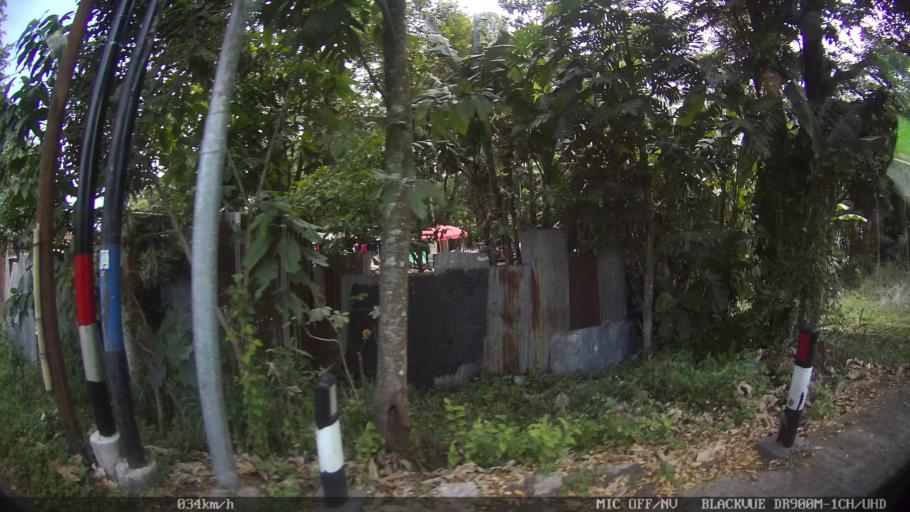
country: ID
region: Central Java
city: Candi Prambanan
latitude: -7.7318
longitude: 110.4581
